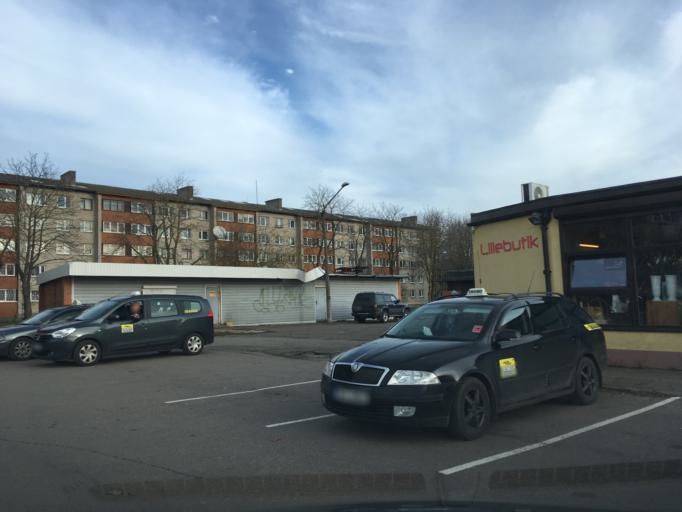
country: EE
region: Ida-Virumaa
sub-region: Narva linn
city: Narva
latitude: 59.3667
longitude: 28.1877
